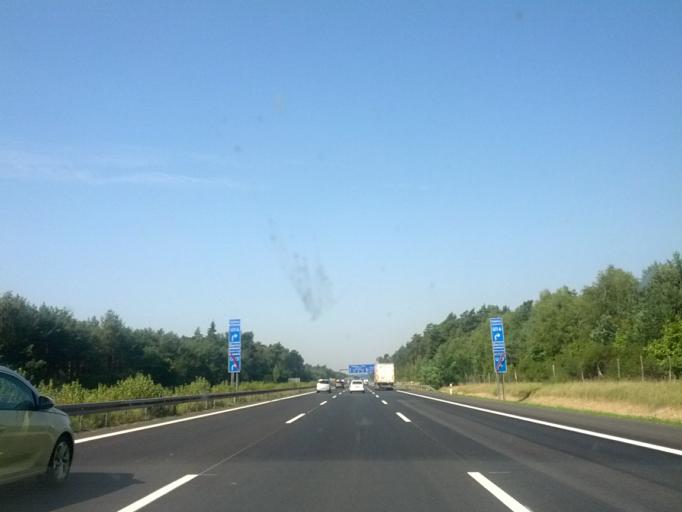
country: DE
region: Brandenburg
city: Ludwigsfelde
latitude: 52.3012
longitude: 13.2289
